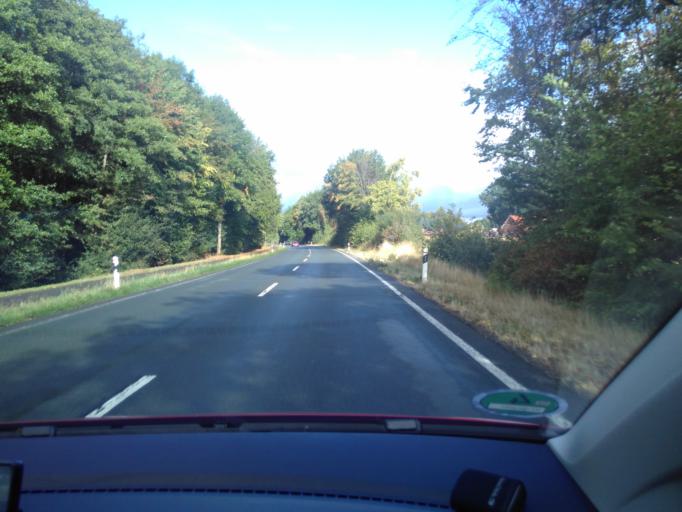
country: DE
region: North Rhine-Westphalia
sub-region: Regierungsbezirk Munster
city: Ostbevern
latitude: 52.0117
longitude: 7.9196
